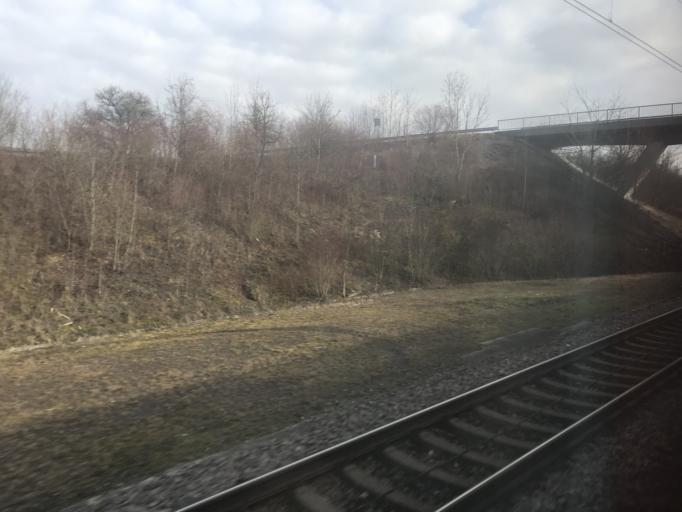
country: DE
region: Baden-Wuerttemberg
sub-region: Regierungsbezirk Stuttgart
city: Markgroningen
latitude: 48.8913
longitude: 9.0772
